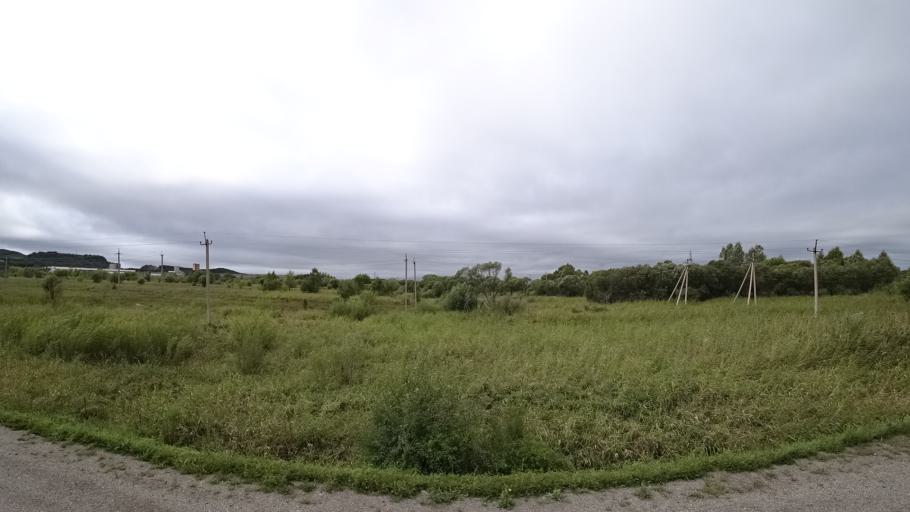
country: RU
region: Primorskiy
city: Monastyrishche
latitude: 44.1749
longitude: 132.4413
